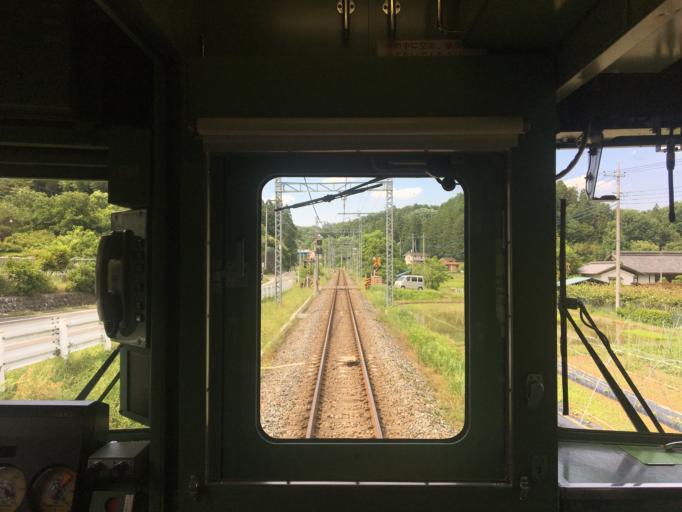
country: JP
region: Saitama
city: Ogawa
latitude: 36.0792
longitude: 139.2377
